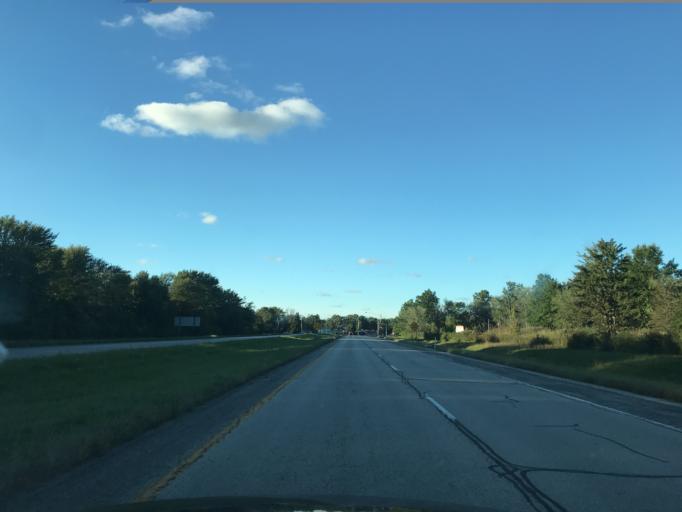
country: US
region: Ohio
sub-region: Ashtabula County
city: Edgewood
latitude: 41.8973
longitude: -80.7819
